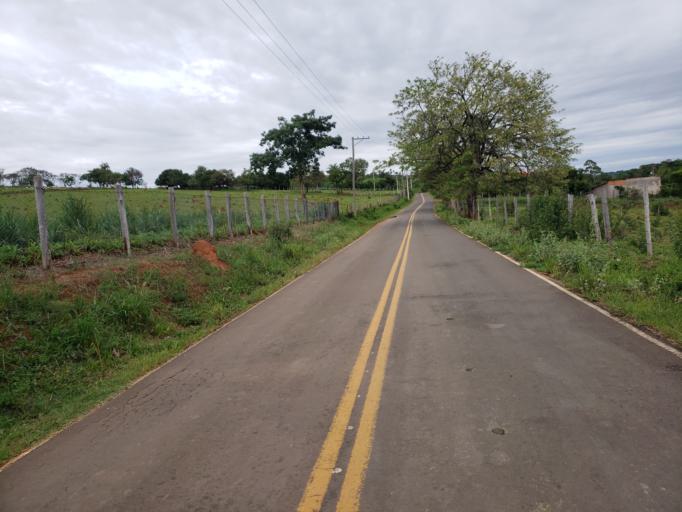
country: BR
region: Sao Paulo
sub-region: Itapira
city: Itapira
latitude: -22.3312
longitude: -46.8211
